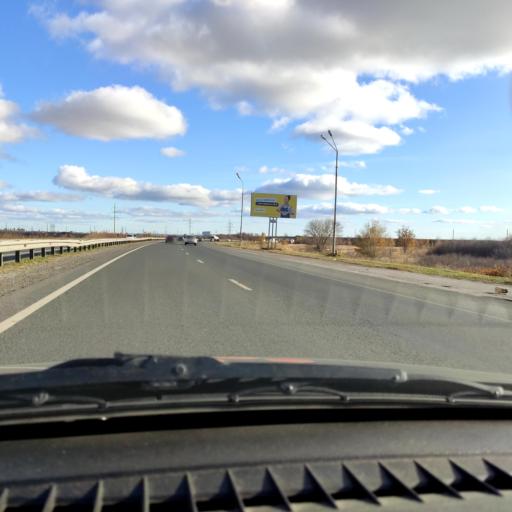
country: RU
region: Samara
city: Tol'yatti
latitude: 53.5671
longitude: 49.4909
